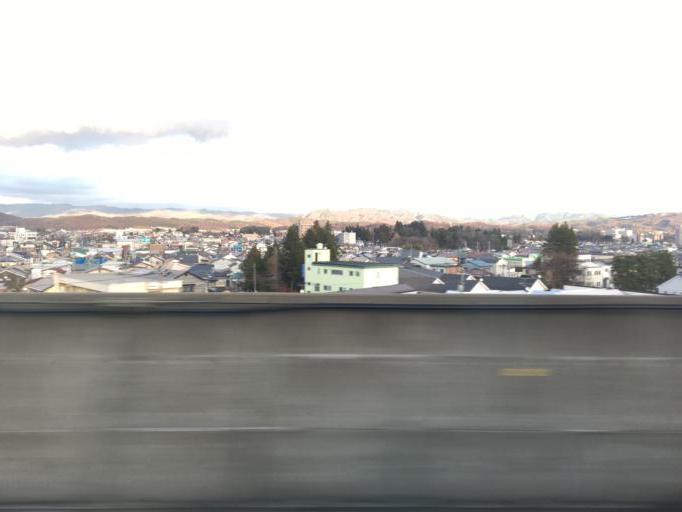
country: JP
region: Iwate
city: Morioka-shi
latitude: 39.7206
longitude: 141.1175
